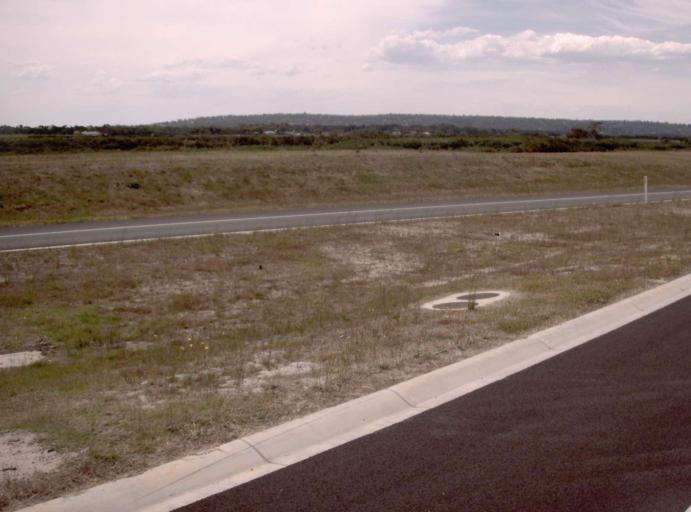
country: AU
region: Victoria
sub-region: Mornington Peninsula
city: Moorooduc
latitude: -38.2491
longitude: 145.1193
